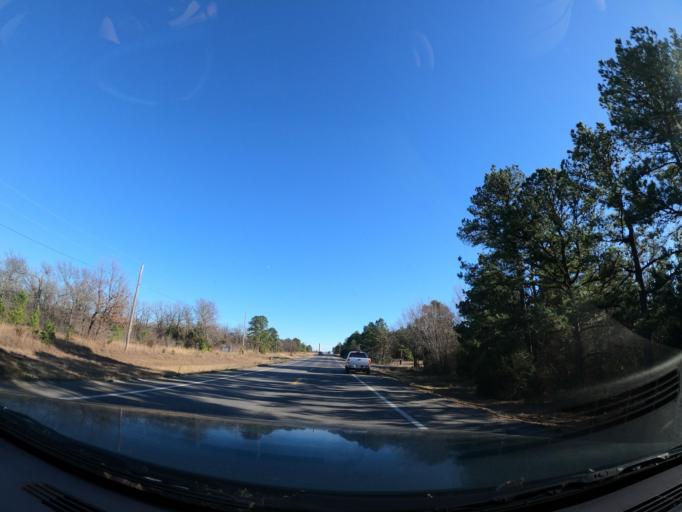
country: US
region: Oklahoma
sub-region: Pittsburg County
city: Longtown
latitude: 35.2323
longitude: -95.4580
